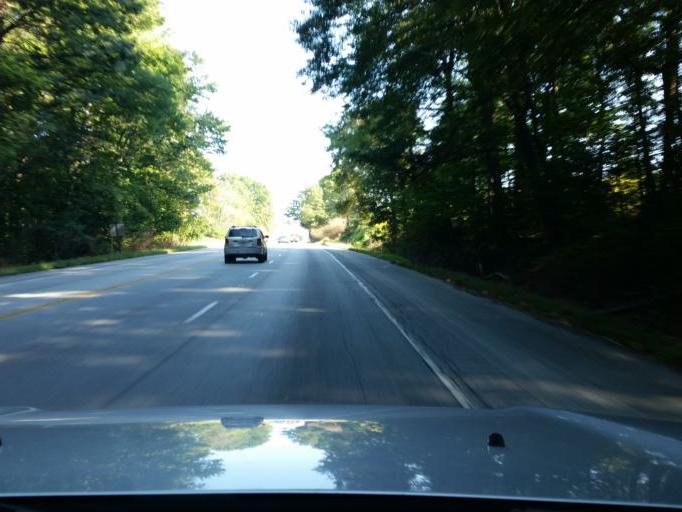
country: US
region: Pennsylvania
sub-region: Chester County
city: Atglen
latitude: 39.9391
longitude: -75.9624
